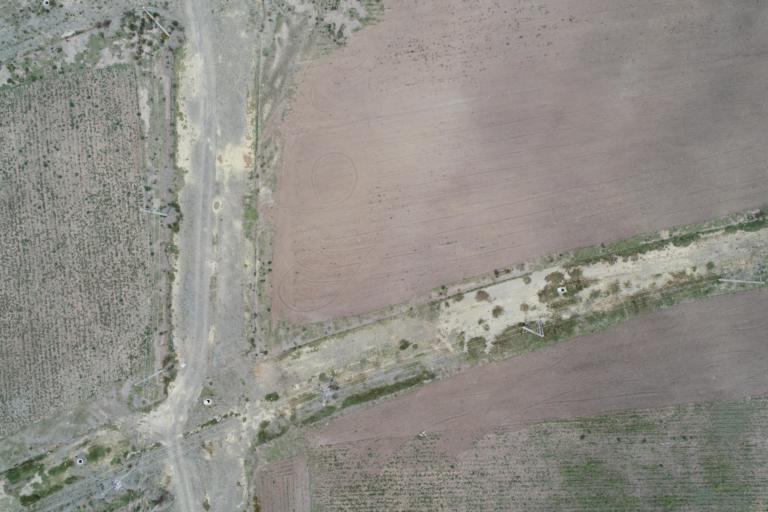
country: BO
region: La Paz
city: La Paz
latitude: -16.5145
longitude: -68.3026
